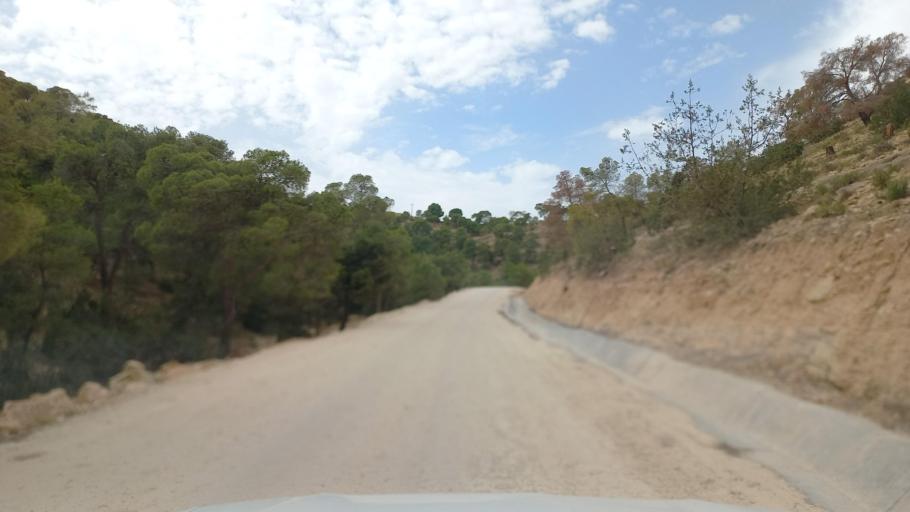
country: TN
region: Al Qasrayn
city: Kasserine
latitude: 35.3777
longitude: 8.8838
